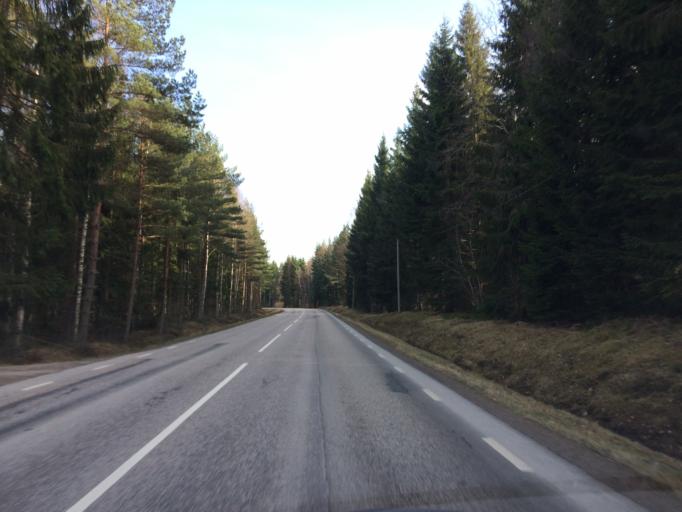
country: SE
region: Kronoberg
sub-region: Almhults Kommun
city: AElmhult
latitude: 56.6020
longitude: 14.0787
